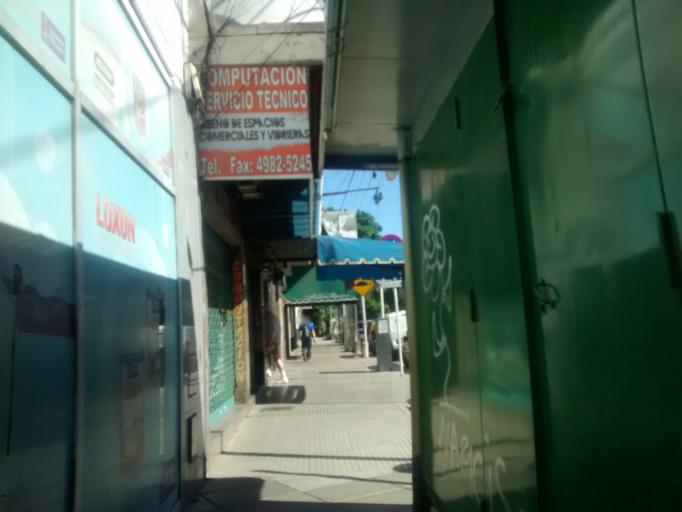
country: AR
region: Buenos Aires F.D.
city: Colegiales
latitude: -34.6079
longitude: -58.4465
